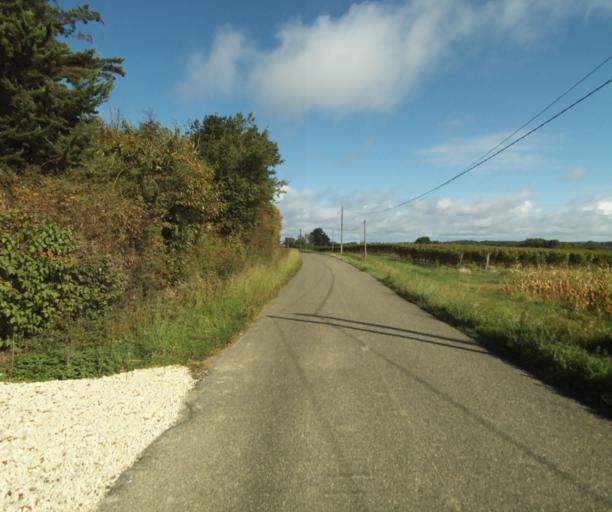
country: FR
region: Midi-Pyrenees
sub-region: Departement du Gers
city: Cazaubon
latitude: 43.8462
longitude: -0.0561
